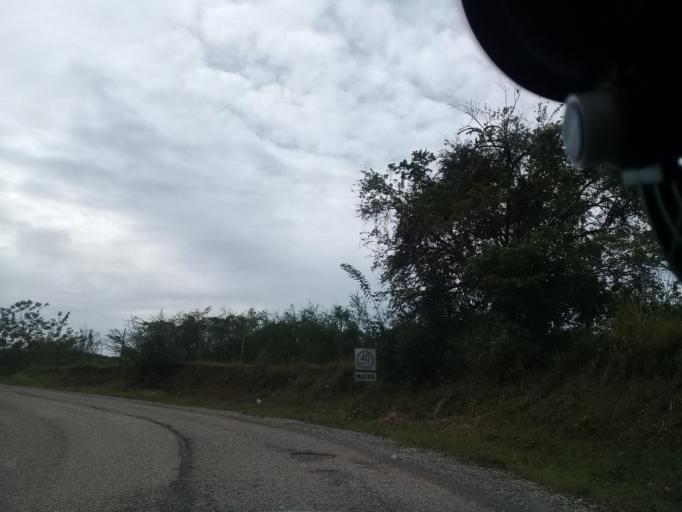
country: MX
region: Veracruz
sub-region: Chalma
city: San Pedro Coyutla
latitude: 21.2150
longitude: -98.3772
